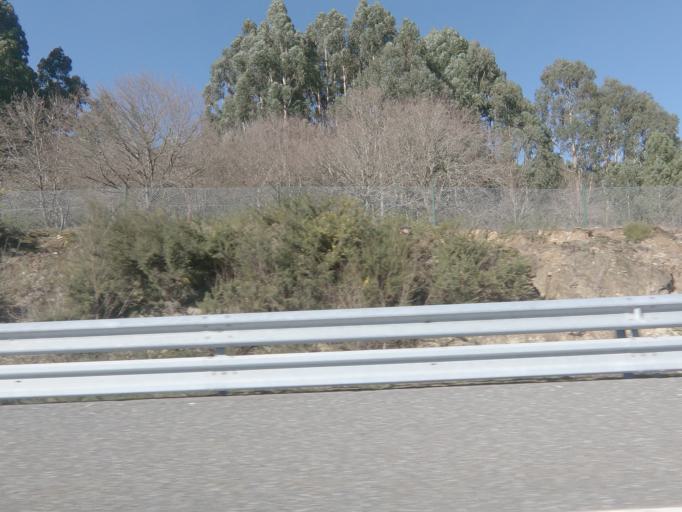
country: ES
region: Galicia
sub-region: Provincia de Pontevedra
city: Dozon
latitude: 42.5464
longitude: -8.0199
